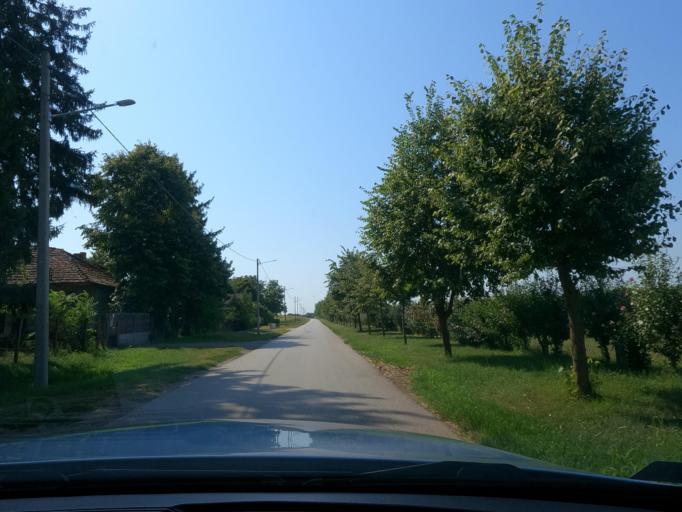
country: HU
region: Csongrad
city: Asotthalom
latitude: 46.0925
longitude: 19.7812
